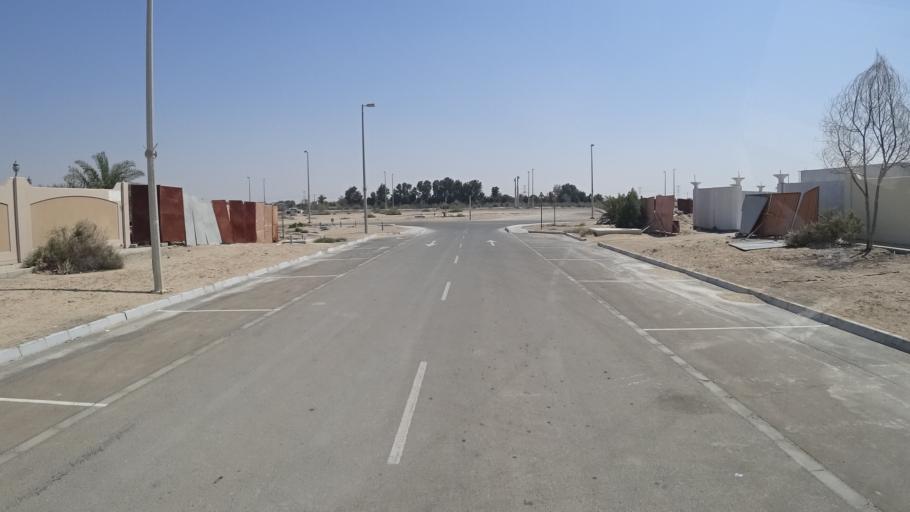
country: AE
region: Abu Dhabi
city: Abu Dhabi
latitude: 24.5448
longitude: 54.6354
